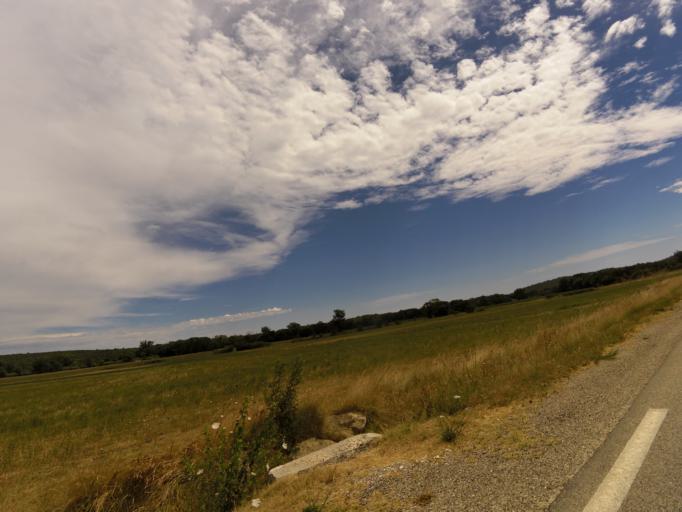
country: FR
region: Languedoc-Roussillon
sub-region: Departement du Gard
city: Quissac
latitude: 43.8860
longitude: 4.0056
